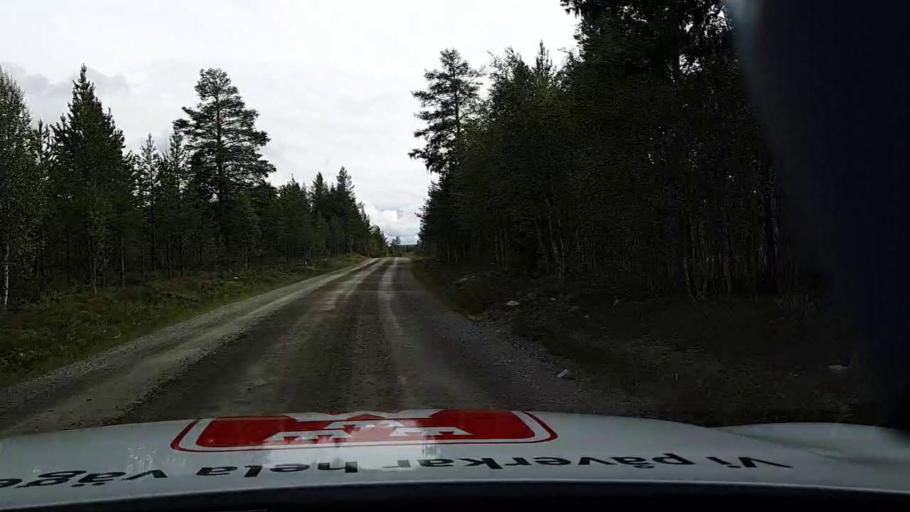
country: SE
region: Jaemtland
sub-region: Are Kommun
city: Jarpen
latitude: 62.5115
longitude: 13.4915
